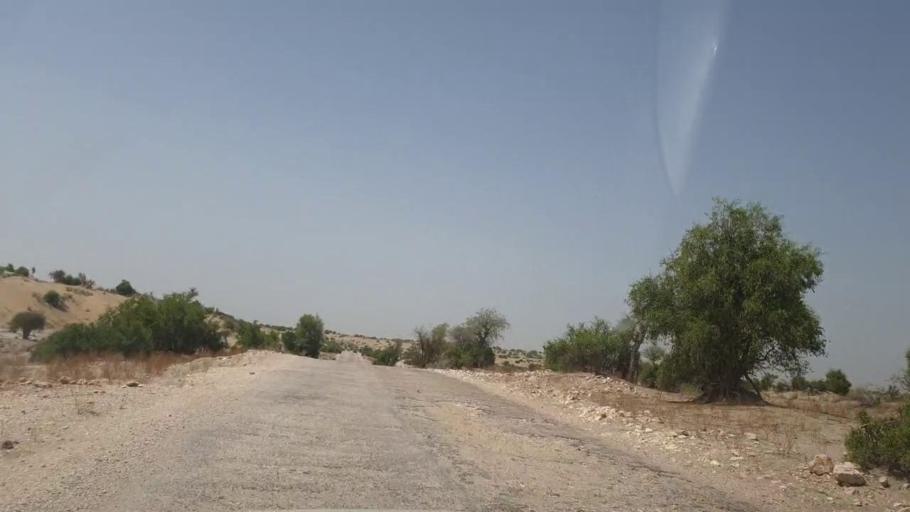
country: PK
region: Sindh
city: Khanpur
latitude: 27.3669
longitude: 69.3168
